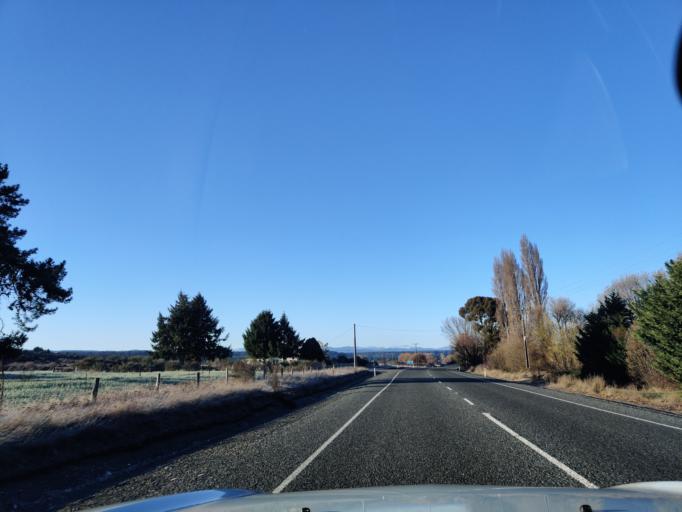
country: NZ
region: Waikato
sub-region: Taupo District
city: Taupo
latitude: -38.7594
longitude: 176.0753
